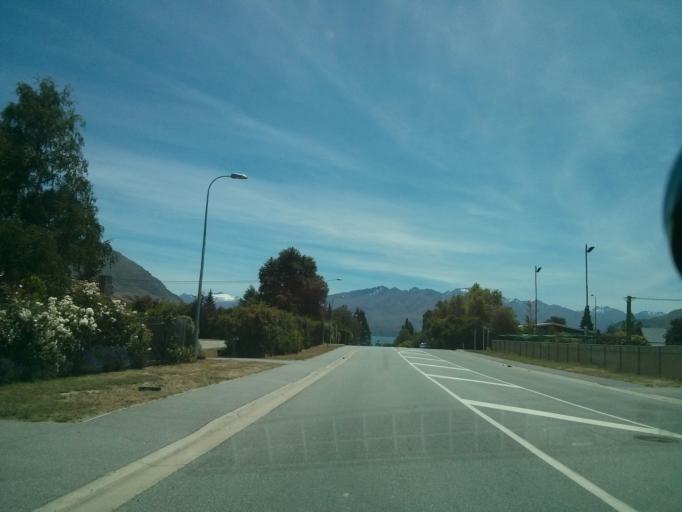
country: NZ
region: Otago
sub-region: Queenstown-Lakes District
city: Wanaka
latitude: -44.7038
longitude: 169.1328
